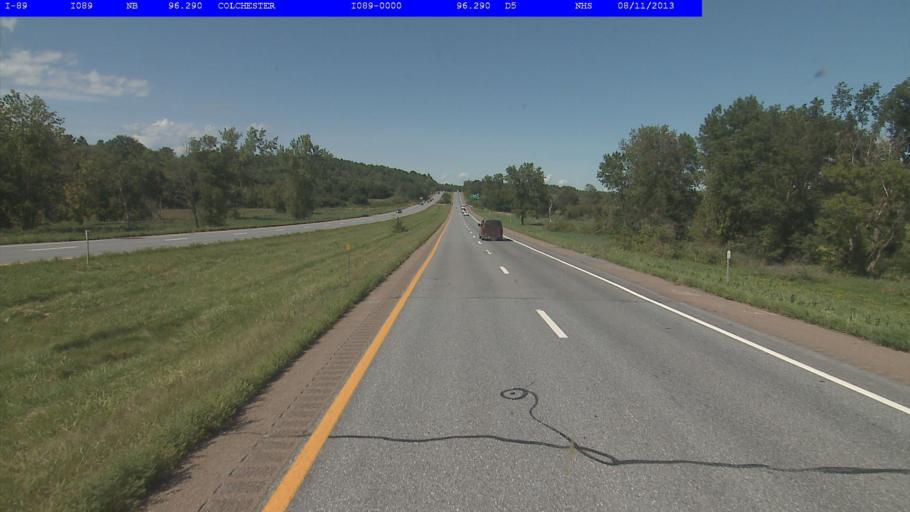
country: US
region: Vermont
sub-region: Chittenden County
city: Colchester
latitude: 44.5678
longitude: -73.1785
